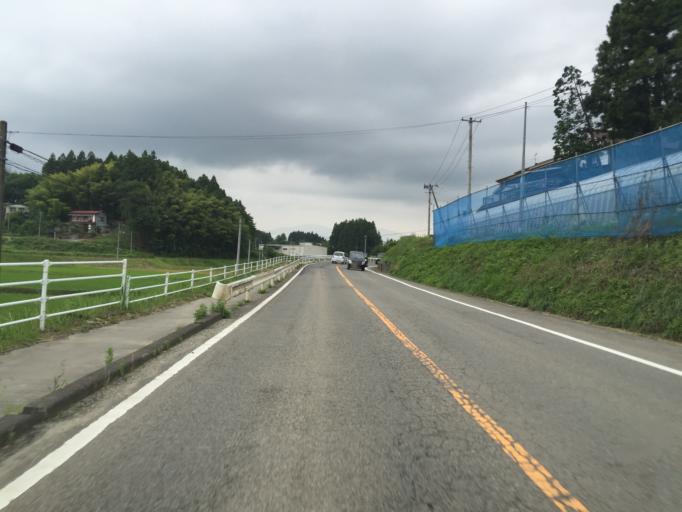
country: JP
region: Fukushima
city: Nihommatsu
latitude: 37.6089
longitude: 140.4828
